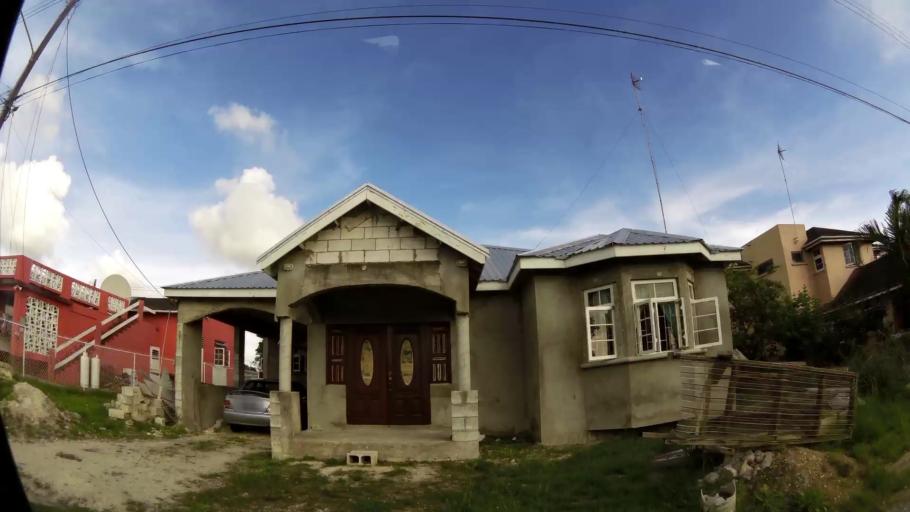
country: BB
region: Christ Church
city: Oistins
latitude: 13.0823
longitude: -59.5653
